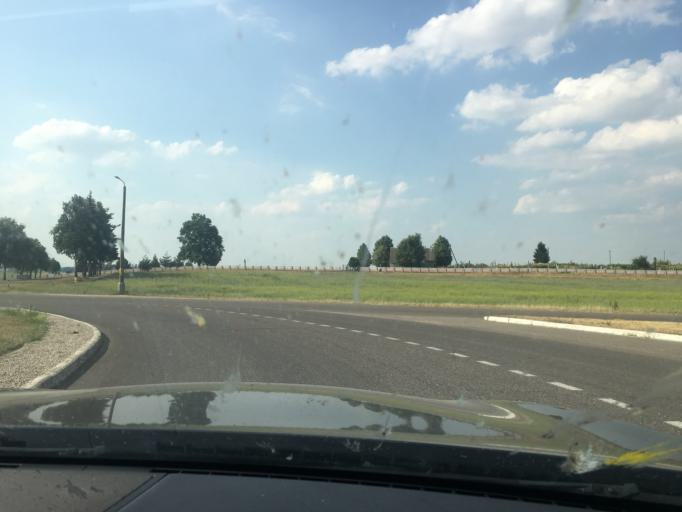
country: BY
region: Grodnenskaya
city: Svislach
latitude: 53.0425
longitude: 24.0864
